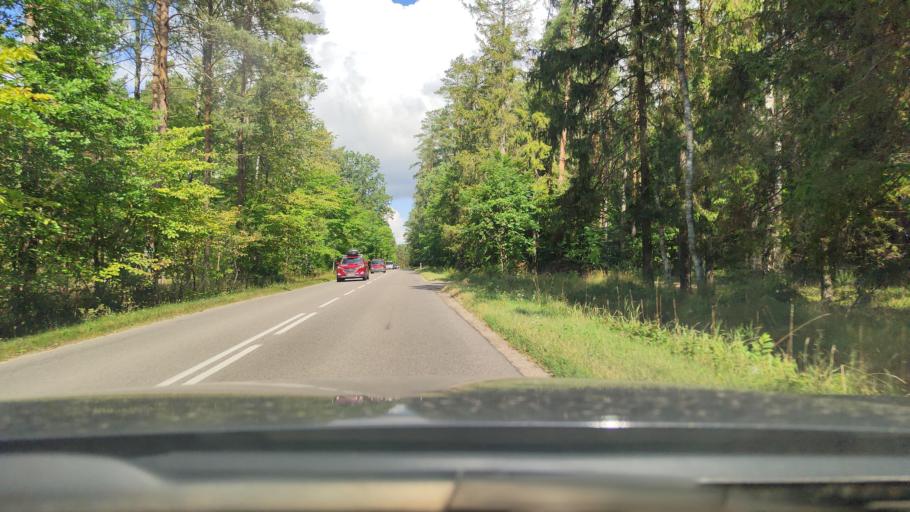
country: PL
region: Pomeranian Voivodeship
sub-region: Powiat wejherowski
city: Wejherowo
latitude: 54.6440
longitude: 18.2174
